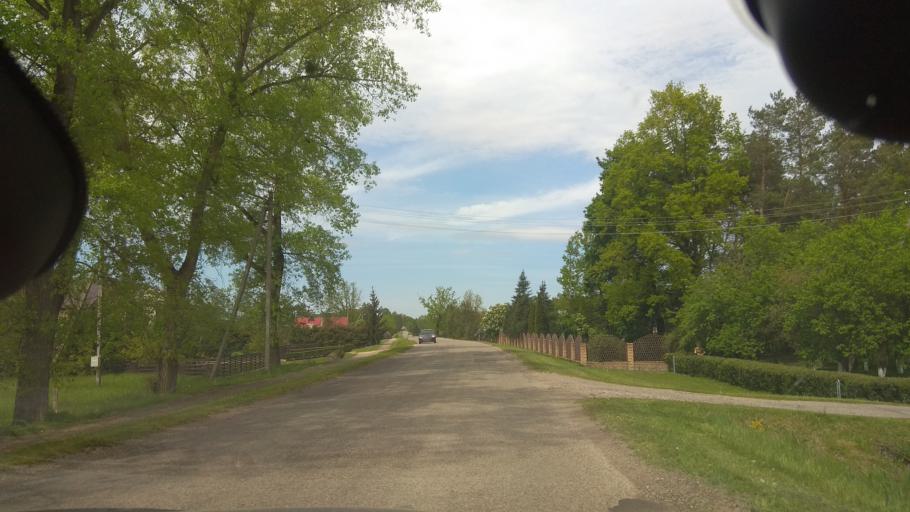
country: LT
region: Vilnius County
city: Ukmerge
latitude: 55.1444
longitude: 24.5852
